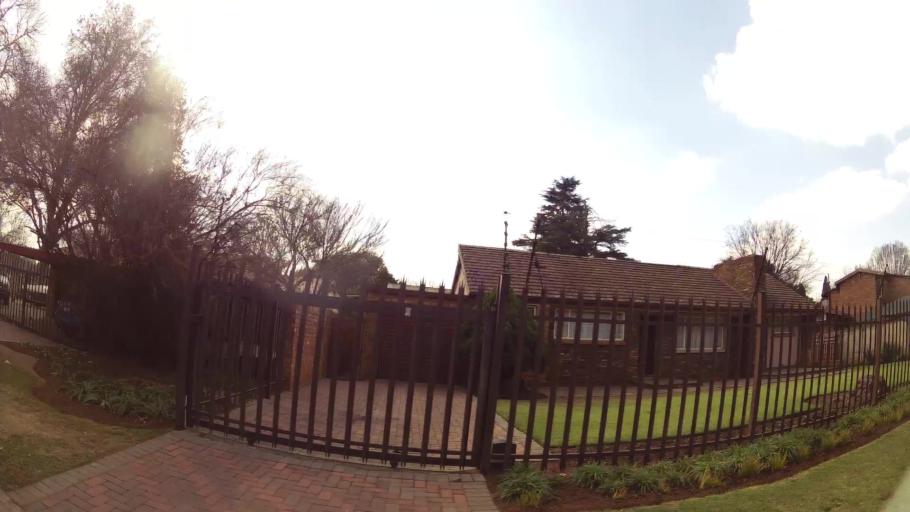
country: ZA
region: Mpumalanga
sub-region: Nkangala District Municipality
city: Delmas
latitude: -26.1458
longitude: 28.6800
